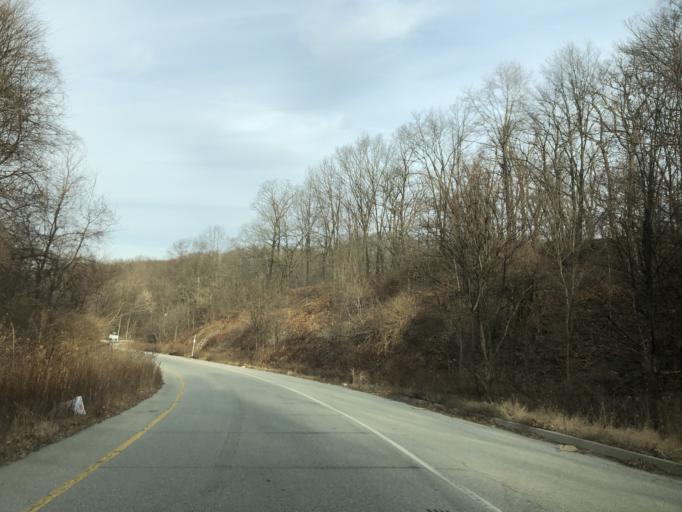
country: US
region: Pennsylvania
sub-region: Chester County
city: Exton
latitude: 40.0131
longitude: -75.6153
